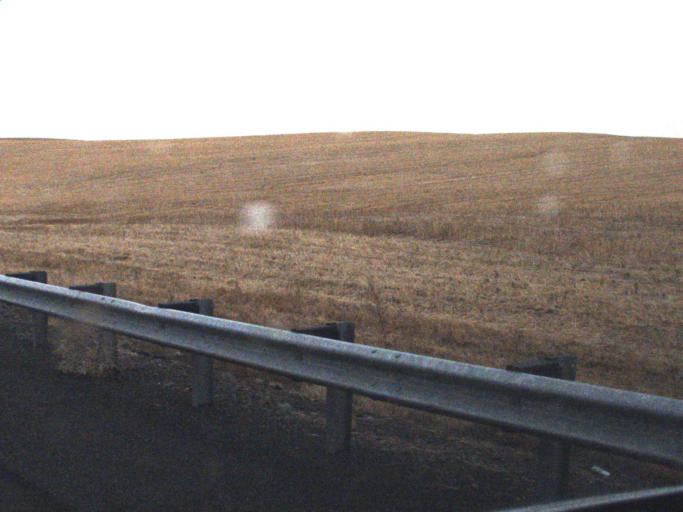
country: US
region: Washington
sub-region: Adams County
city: Ritzville
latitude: 46.7915
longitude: -118.3884
